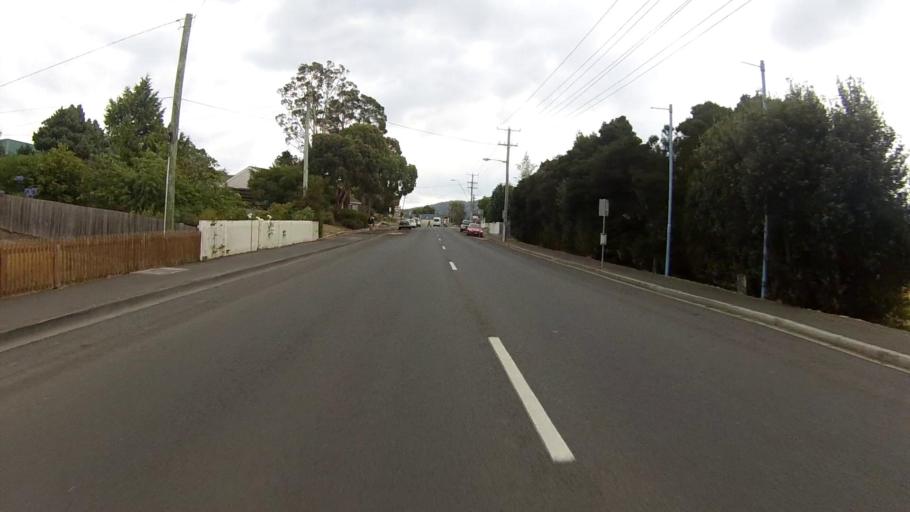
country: AU
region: Tasmania
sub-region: Huon Valley
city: Cygnet
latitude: -43.1596
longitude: 147.0755
